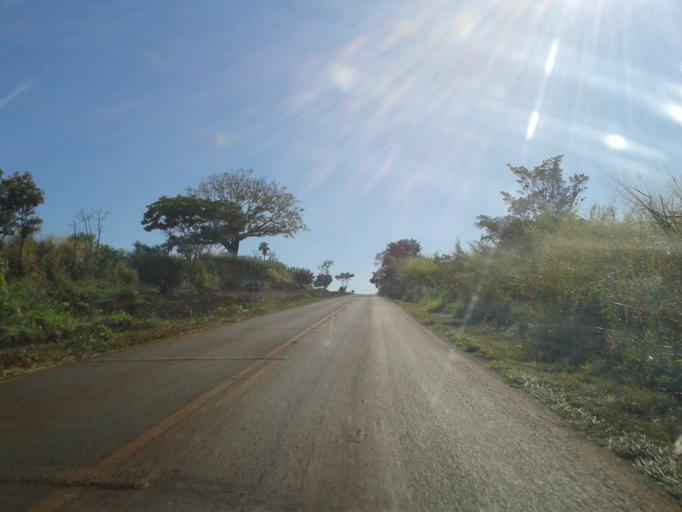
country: BR
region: Minas Gerais
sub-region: Capinopolis
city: Capinopolis
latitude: -18.6726
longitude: -49.5624
